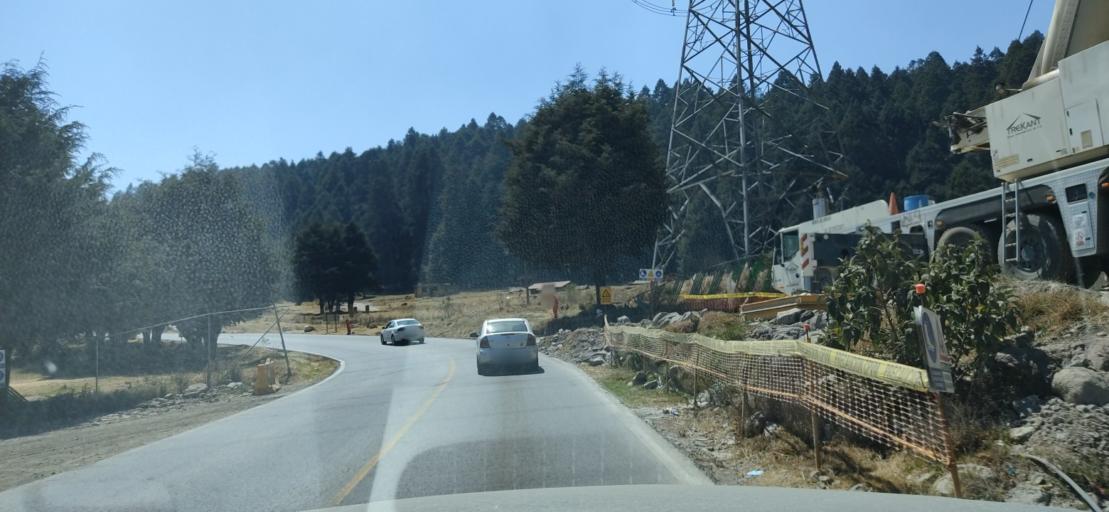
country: MX
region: Mexico
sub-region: Ocoyoacac
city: San Jeronimo Acazulco
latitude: 19.2946
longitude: -99.3753
